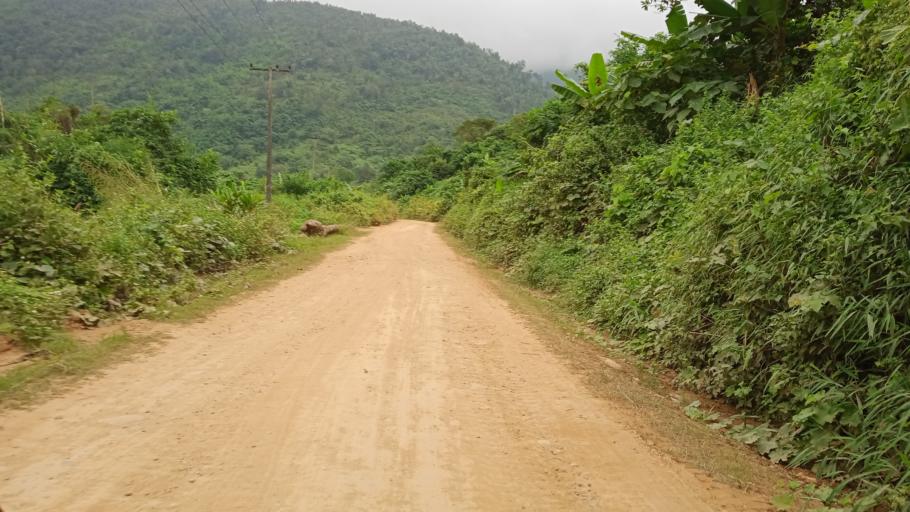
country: LA
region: Xiangkhoang
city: Phonsavan
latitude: 19.0931
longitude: 102.9873
